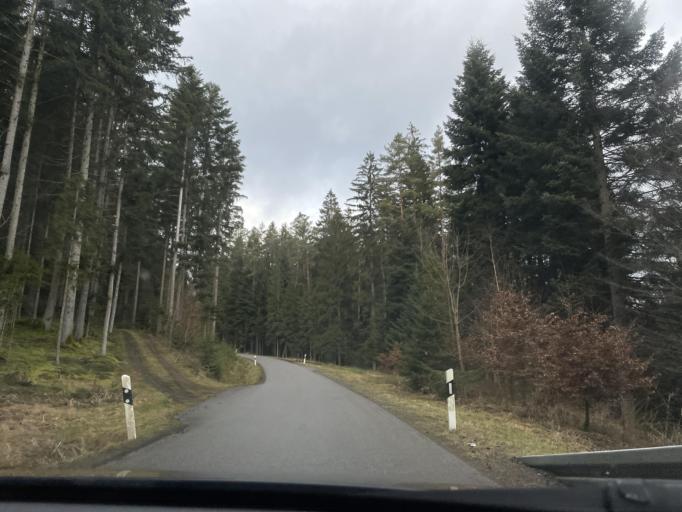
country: DE
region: Bavaria
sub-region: Lower Bavaria
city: Prackenbach
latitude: 49.1238
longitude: 12.8390
